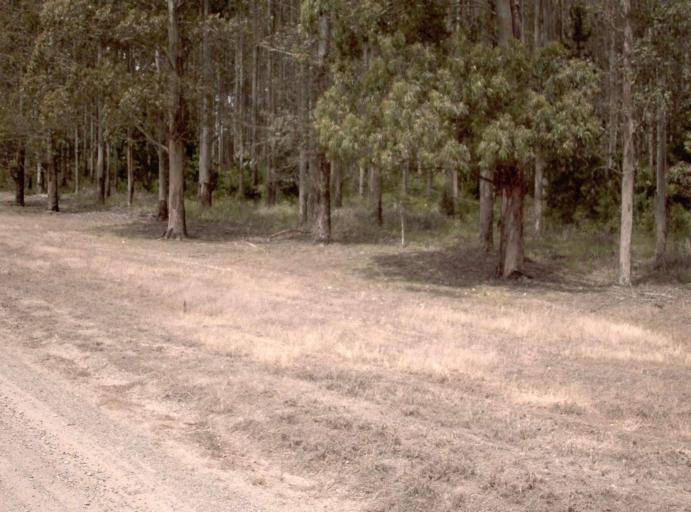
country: AU
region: Victoria
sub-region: Latrobe
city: Traralgon
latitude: -38.3779
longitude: 146.6744
